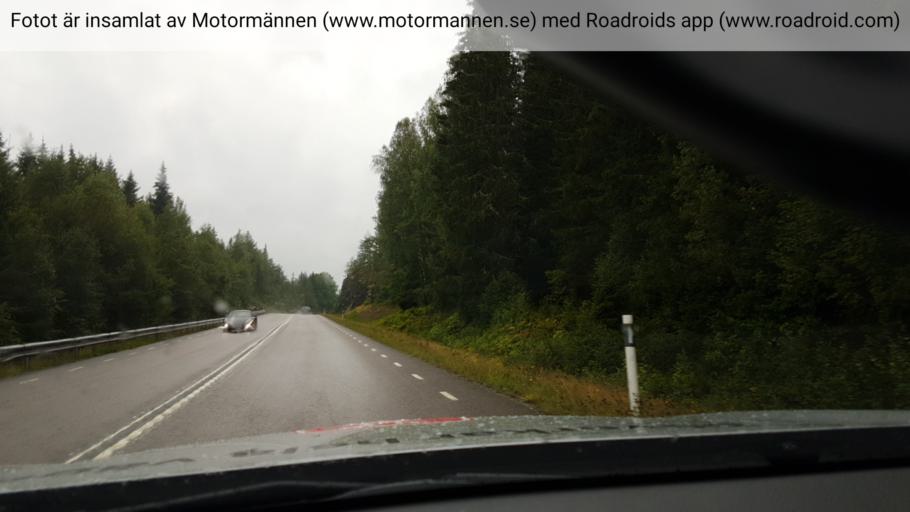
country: SE
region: Vaestra Goetaland
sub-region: Dals-Ed Kommun
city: Ed
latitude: 58.9333
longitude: 12.0442
